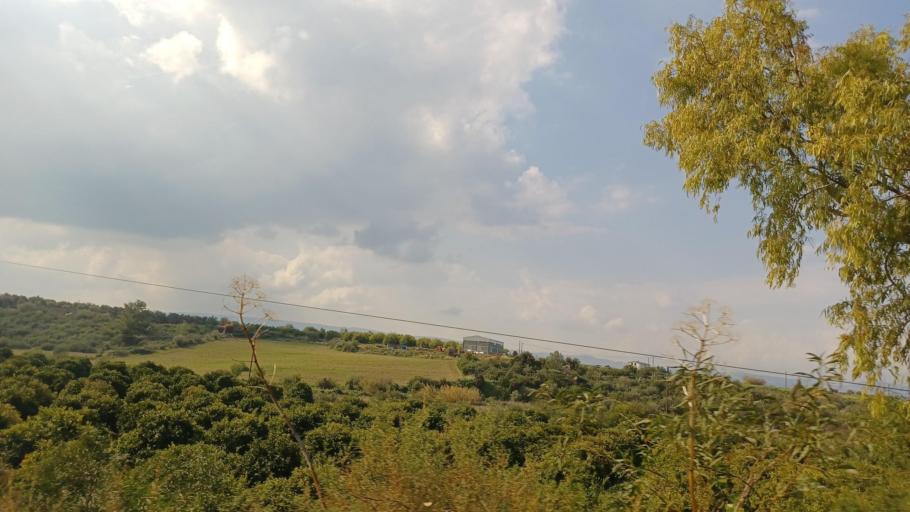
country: CY
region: Pafos
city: Polis
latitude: 35.0481
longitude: 32.4603
